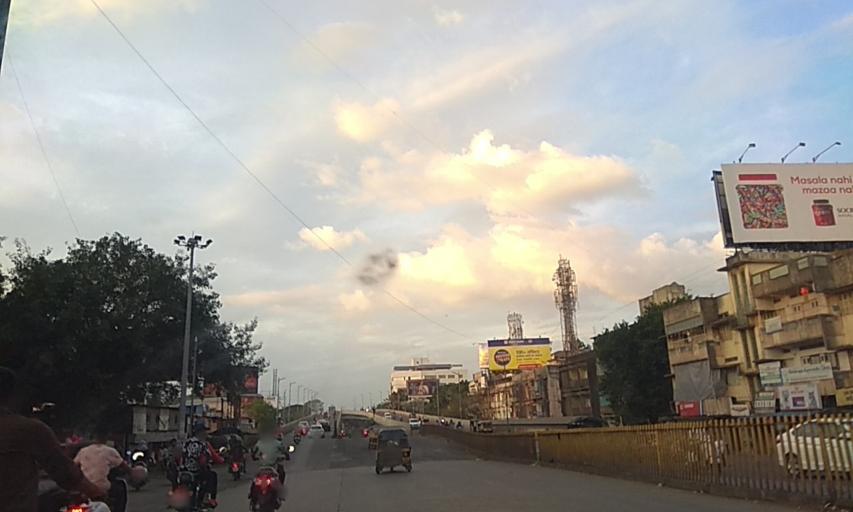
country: IN
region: Maharashtra
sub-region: Pune Division
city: Pune
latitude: 18.4939
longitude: 73.8578
